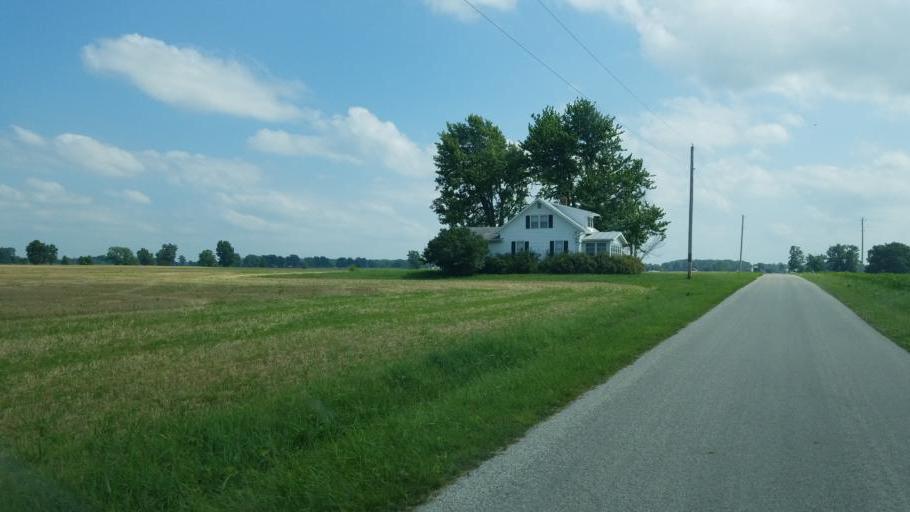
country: US
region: Ohio
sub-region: Huron County
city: Willard
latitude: 40.9723
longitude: -82.7623
